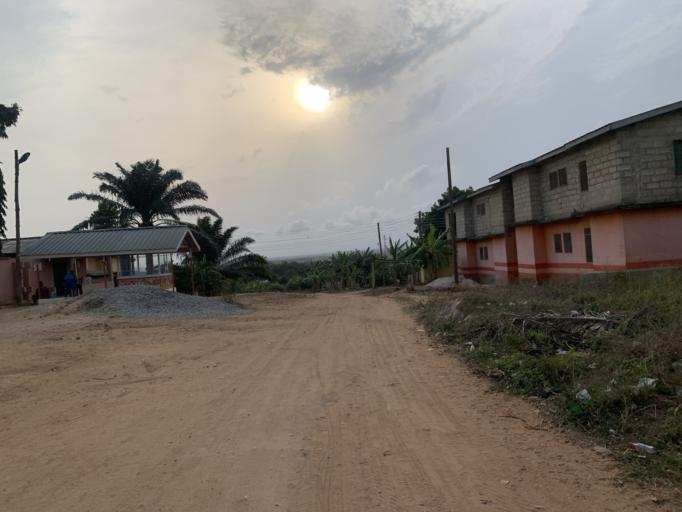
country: GH
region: Central
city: Winneba
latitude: 5.3598
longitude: -0.6274
